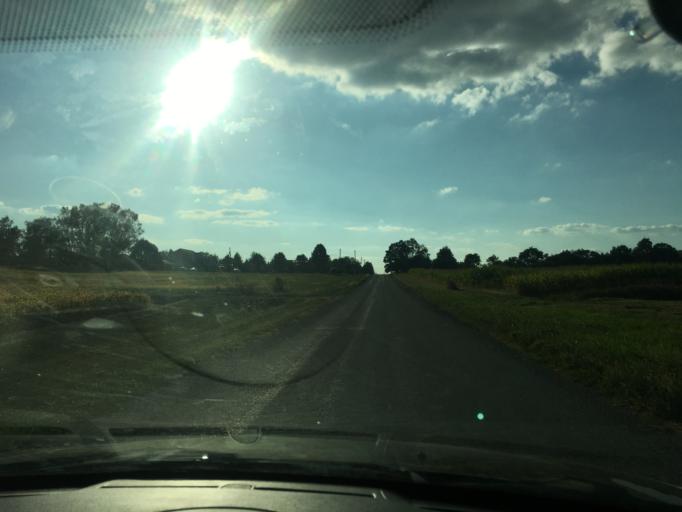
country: US
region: Ohio
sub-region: Logan County
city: West Liberty
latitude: 40.1845
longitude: -83.7487
